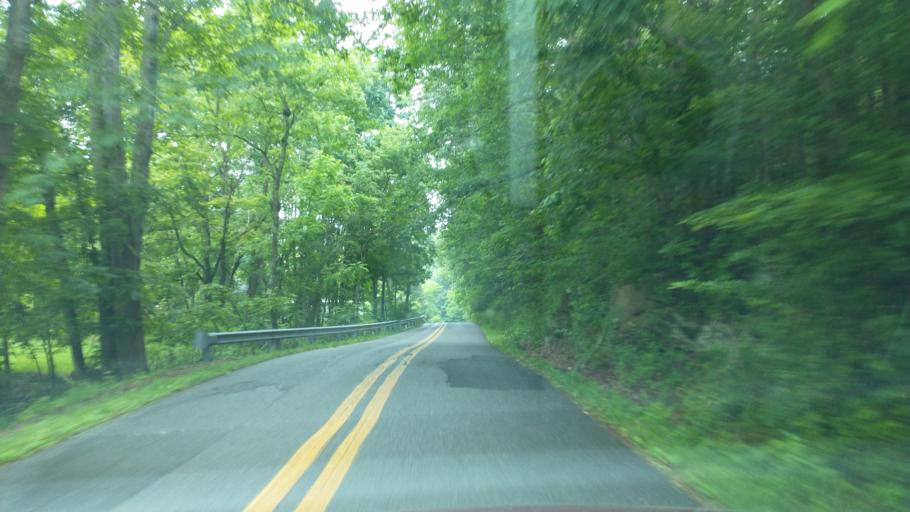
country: US
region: West Virginia
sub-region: Mercer County
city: Athens
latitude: 37.4344
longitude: -80.9747
